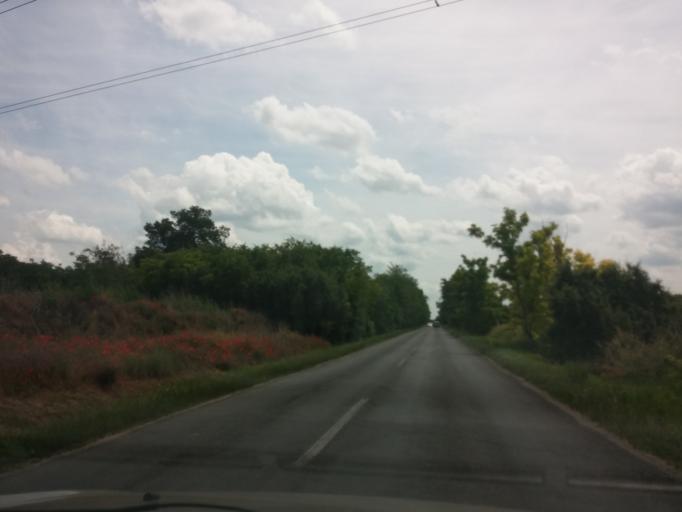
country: HU
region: Pest
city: Szigetcsep
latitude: 47.2897
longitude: 18.9822
